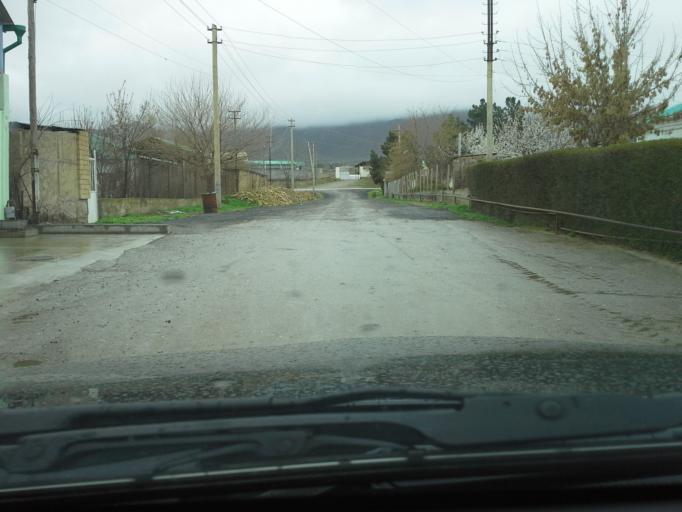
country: TM
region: Ahal
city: Abadan
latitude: 37.9673
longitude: 58.2060
